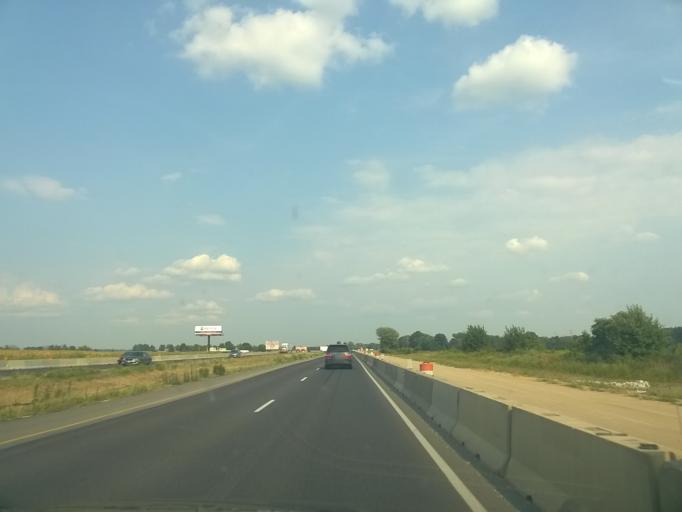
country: US
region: Indiana
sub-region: Vigo County
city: Seelyville
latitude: 39.4305
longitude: -87.3212
